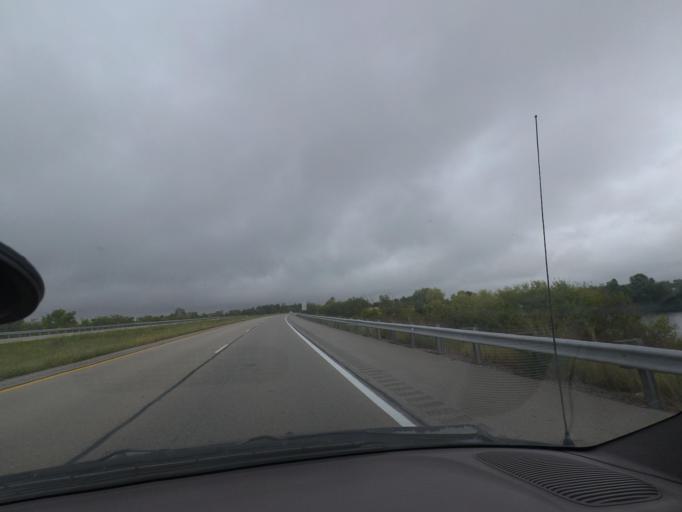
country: US
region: Illinois
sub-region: Piatt County
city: Monticello
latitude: 40.0878
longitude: -88.5215
